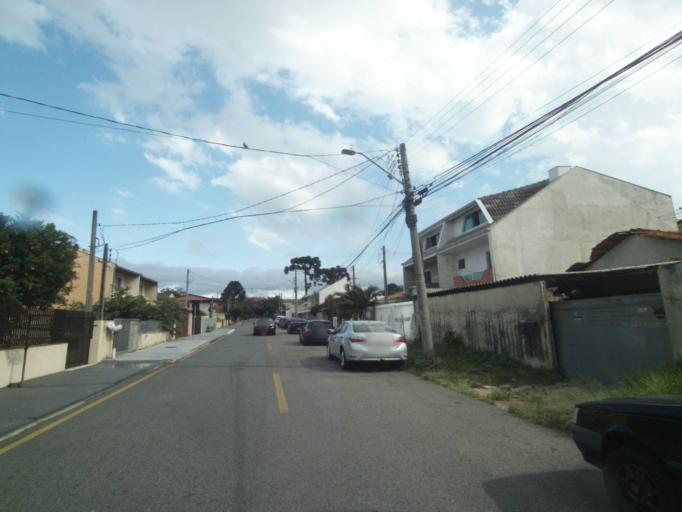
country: BR
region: Parana
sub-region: Pinhais
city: Pinhais
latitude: -25.4469
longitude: -49.2163
